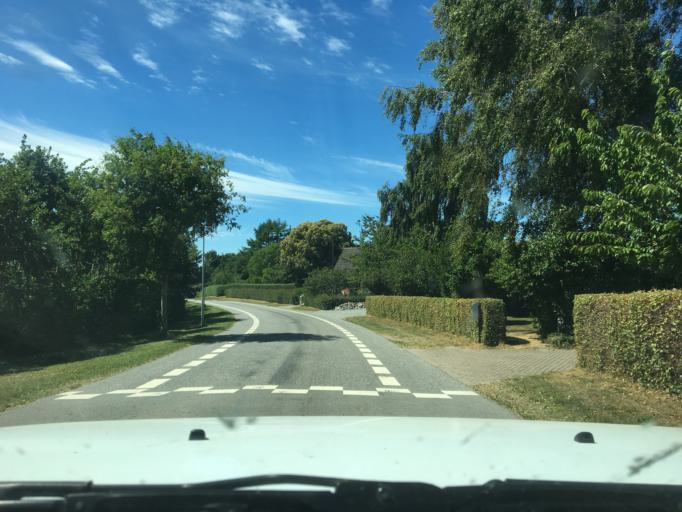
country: DK
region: Central Jutland
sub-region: Syddjurs Kommune
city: Hornslet
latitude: 56.3328
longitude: 10.3835
